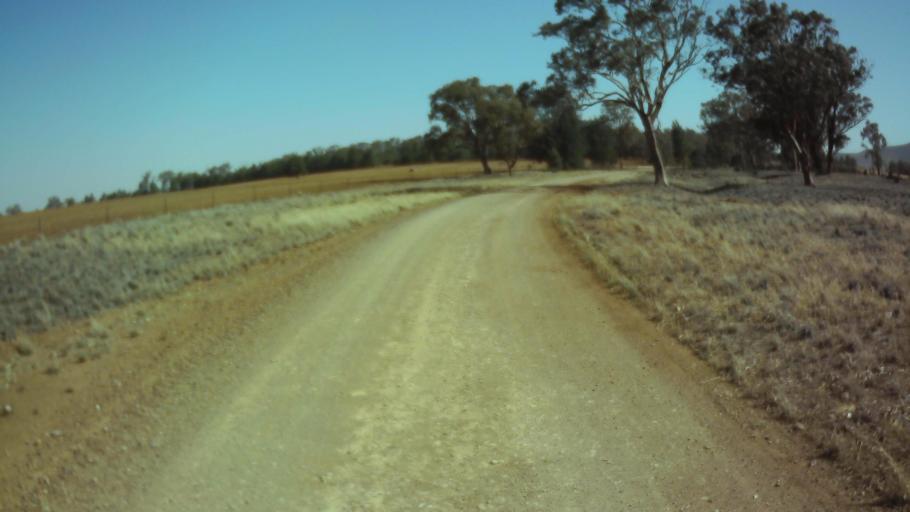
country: AU
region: New South Wales
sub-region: Weddin
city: Grenfell
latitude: -33.8567
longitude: 148.0156
